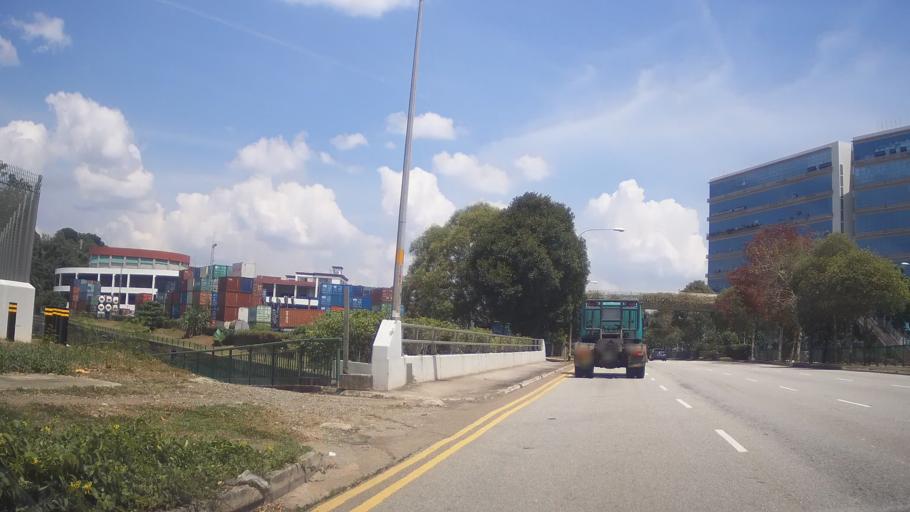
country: SG
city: Singapore
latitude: 1.3141
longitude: 103.7008
